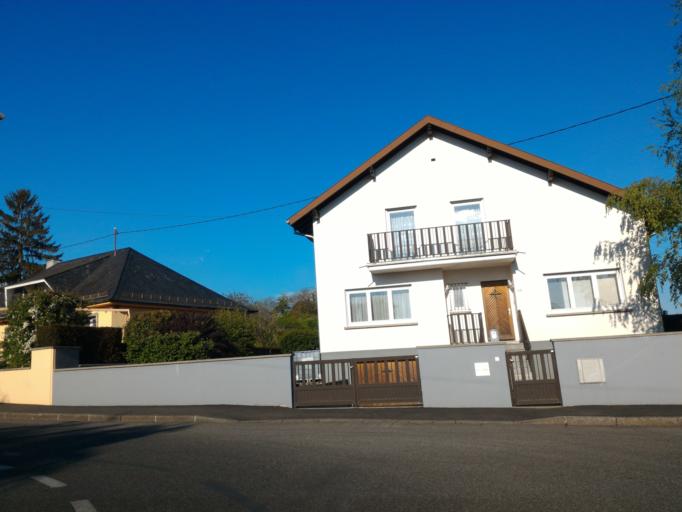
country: FR
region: Alsace
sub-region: Departement du Haut-Rhin
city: Riedisheim
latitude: 47.7494
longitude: 7.3748
